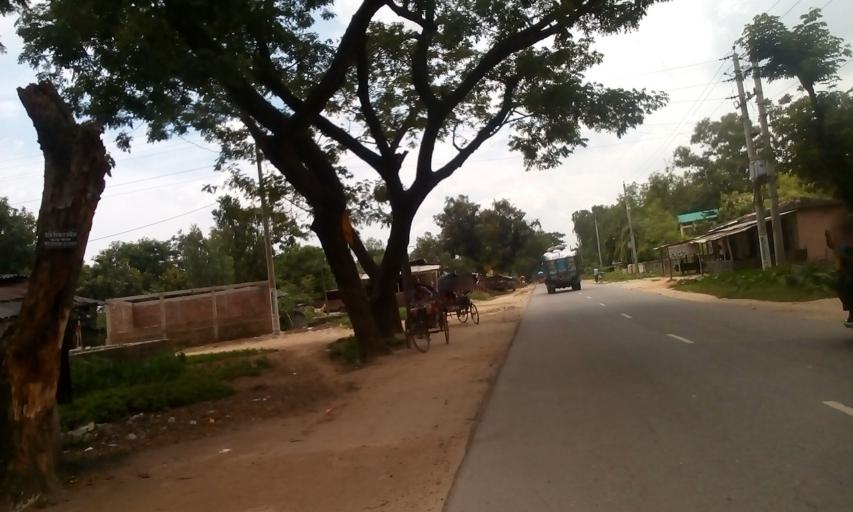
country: BD
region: Rangpur Division
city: Parbatipur
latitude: 25.3969
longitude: 88.9878
